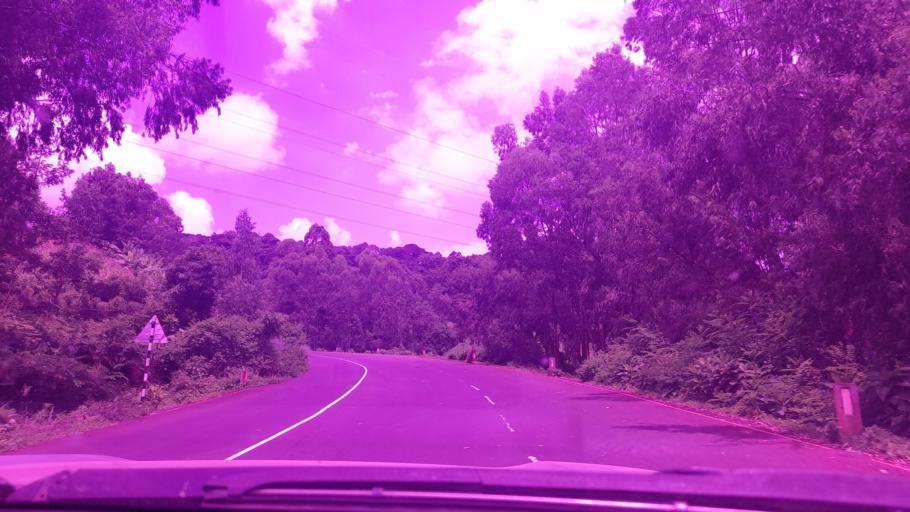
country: ET
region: Oromiya
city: Metu
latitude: 8.3359
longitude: 35.7508
